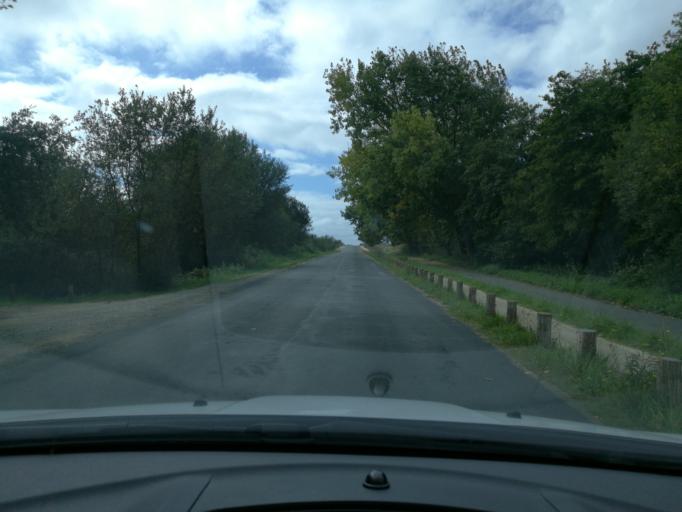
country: FR
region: Poitou-Charentes
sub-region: Departement de la Charente-Maritime
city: Saint-Trojan-les-Bains
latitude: 45.8555
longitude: -1.2455
